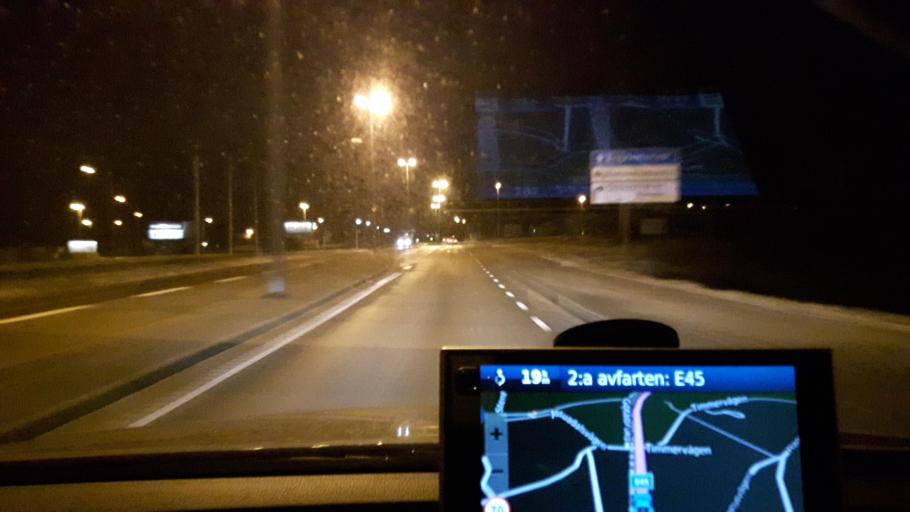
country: SE
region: Vaestra Goetaland
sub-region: Lilla Edets Kommun
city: Lilla Edet
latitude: 58.1075
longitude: 12.1487
